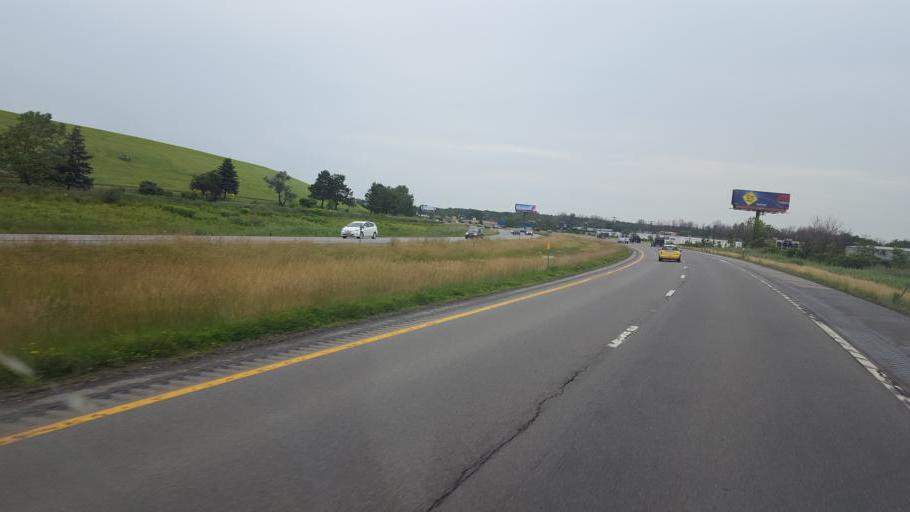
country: US
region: New York
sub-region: Niagara County
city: Niagara Falls
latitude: 43.0996
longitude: -78.9820
